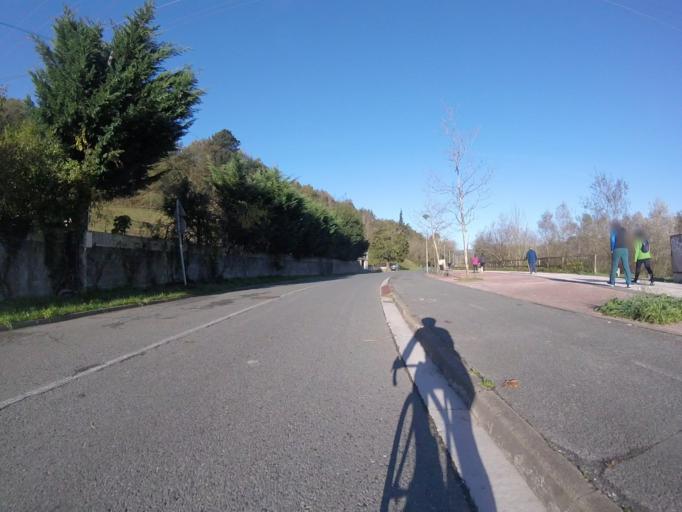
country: ES
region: Basque Country
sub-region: Provincia de Guipuzcoa
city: Lasarte
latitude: 43.2678
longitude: -2.0256
